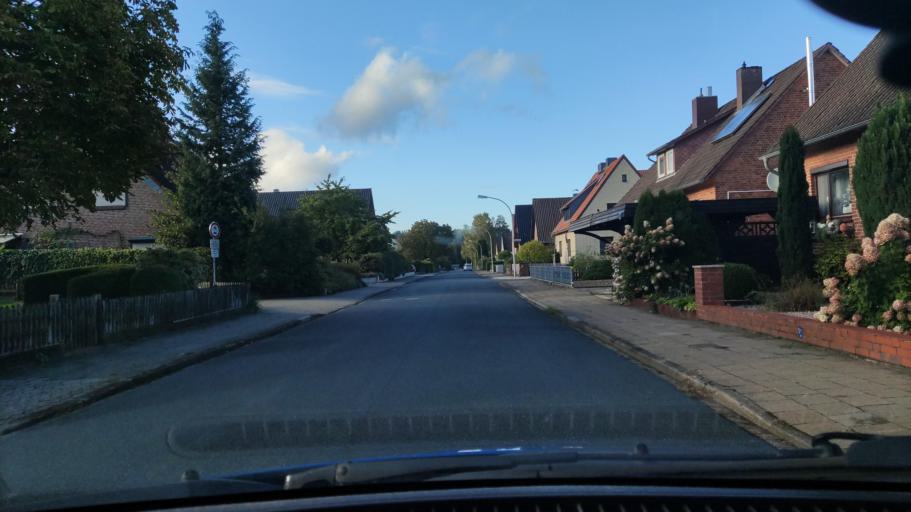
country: DE
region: Lower Saxony
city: Munster
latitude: 52.9946
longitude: 10.1026
